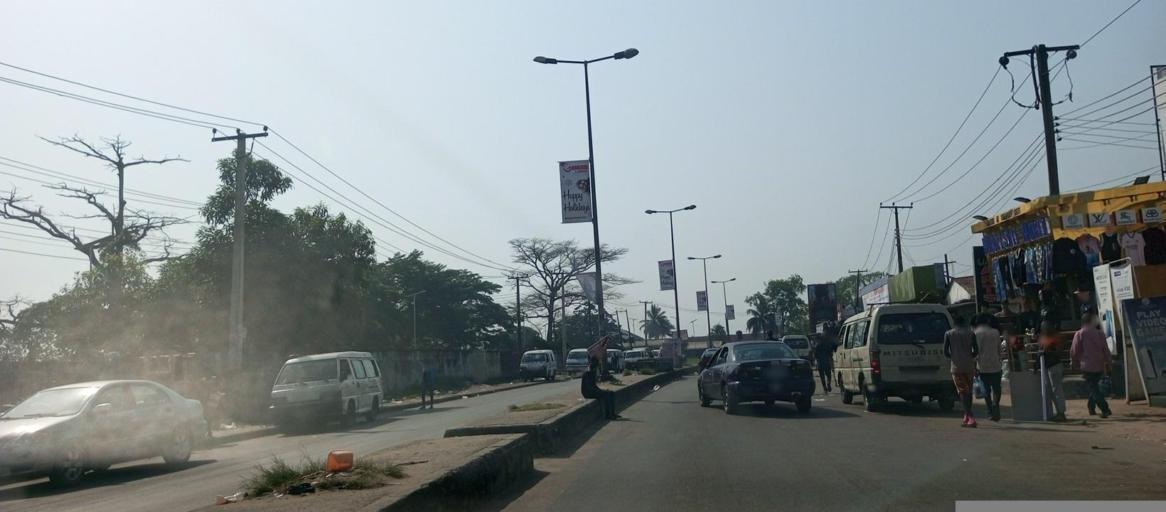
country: NG
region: Rivers
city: Emuoha
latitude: 4.8965
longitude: 6.9070
